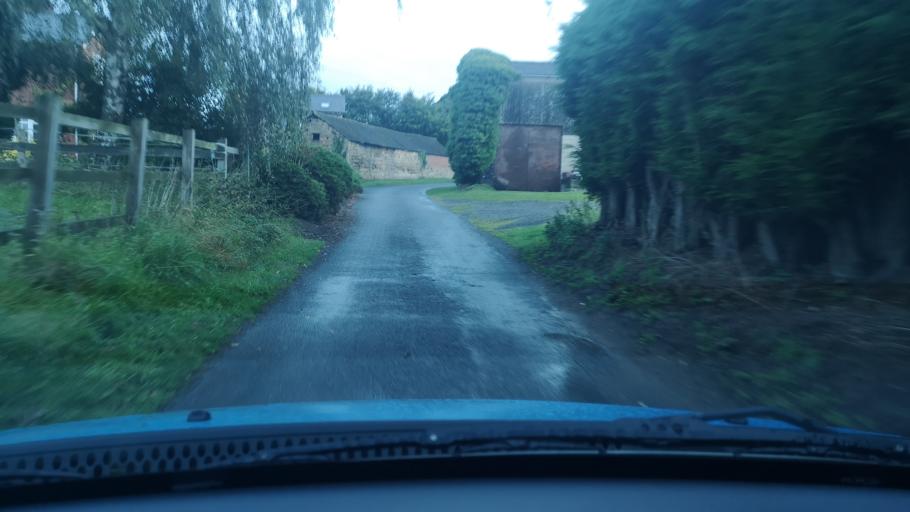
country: GB
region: England
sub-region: City and Borough of Wakefield
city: Low Ackworth
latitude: 53.6597
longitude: -1.3129
